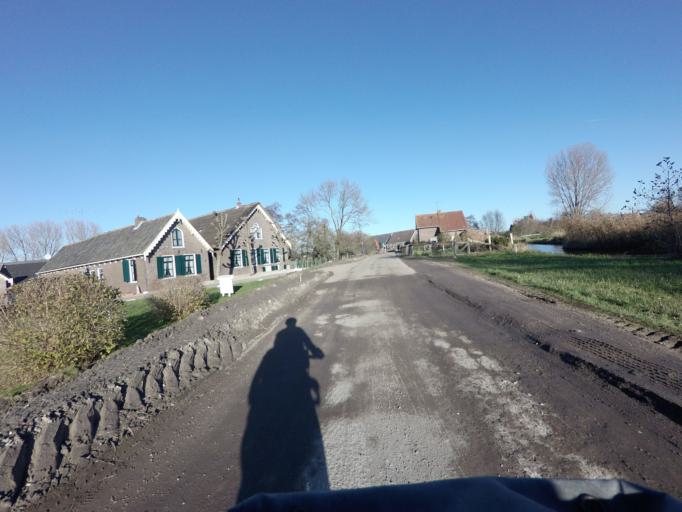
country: NL
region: North Holland
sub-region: Gemeente Amsterdam
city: Amsterdam-Zuidoost
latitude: 52.2600
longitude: 4.9602
